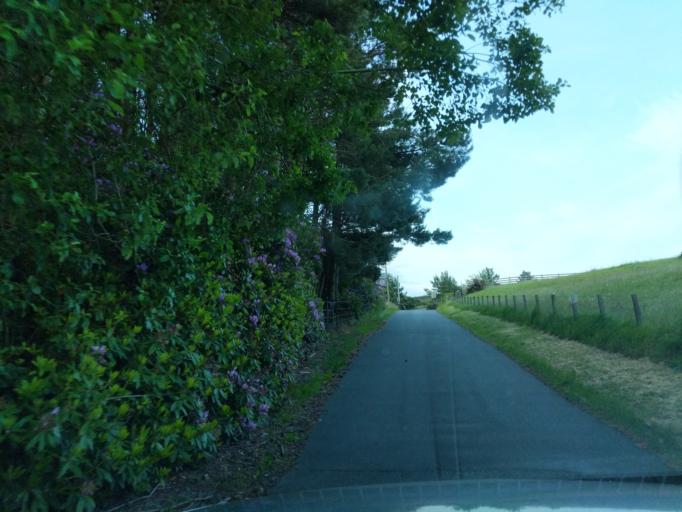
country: GB
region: Scotland
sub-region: Midlothian
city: Bonnyrigg
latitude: 55.7790
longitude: -3.1136
